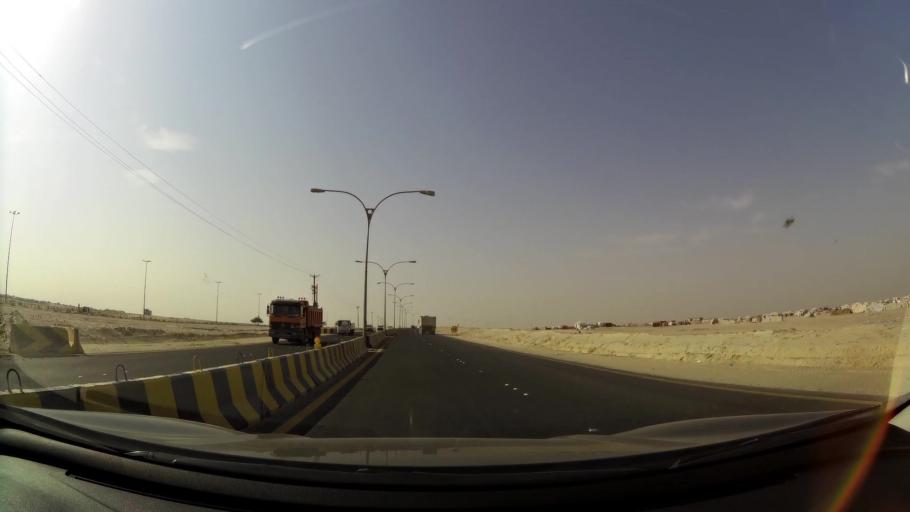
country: KW
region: Al Ahmadi
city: Al Ahmadi
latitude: 28.8986
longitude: 48.0890
